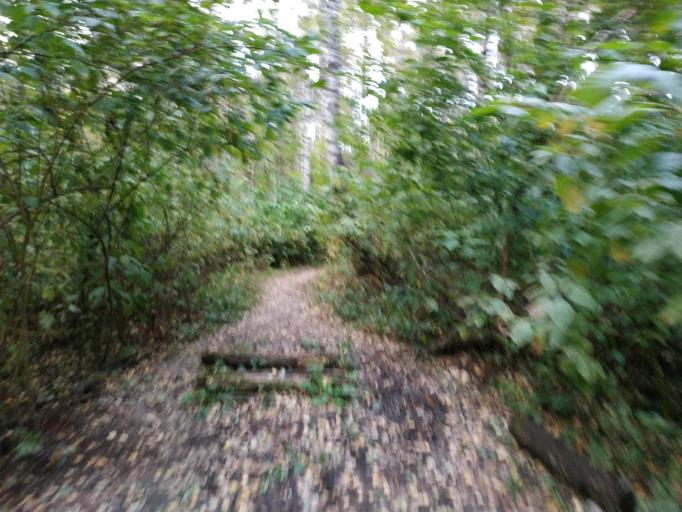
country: RU
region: Moscow
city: Khimki
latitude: 55.8717
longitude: 37.4315
